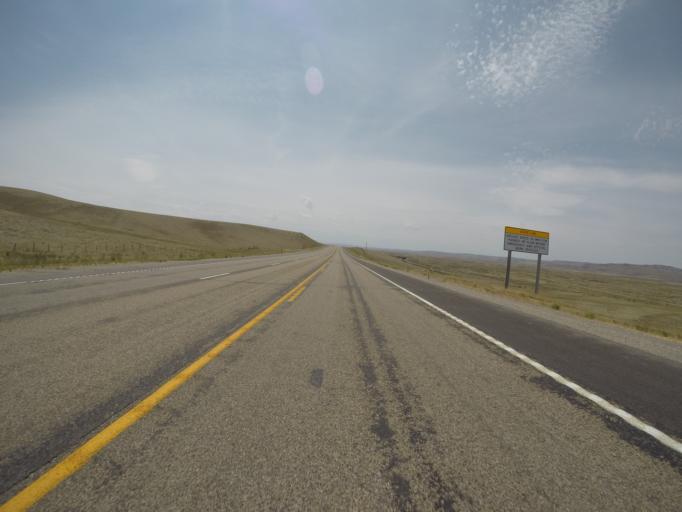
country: US
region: Wyoming
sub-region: Lincoln County
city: Kemmerer
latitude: 41.7651
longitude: -110.5593
